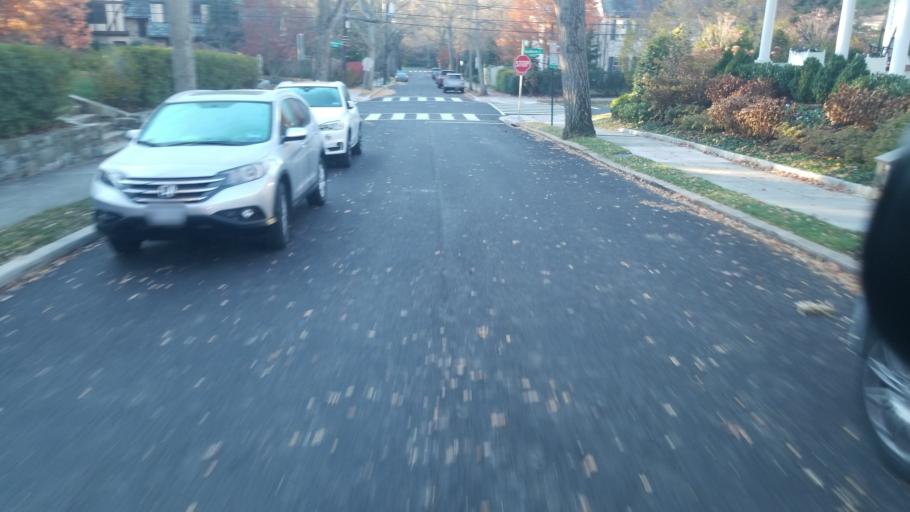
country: US
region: Maryland
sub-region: Montgomery County
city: Friendship Village
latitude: 38.9293
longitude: -77.0874
